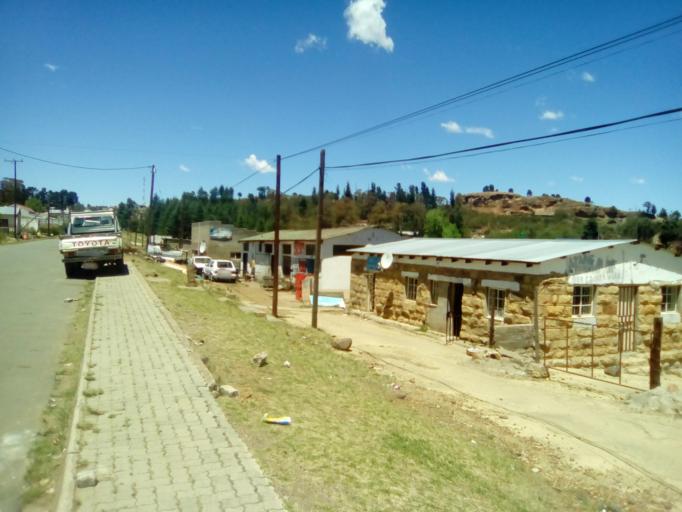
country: LS
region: Qacha's Nek
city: Qacha's Nek
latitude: -30.1176
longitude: 28.6913
